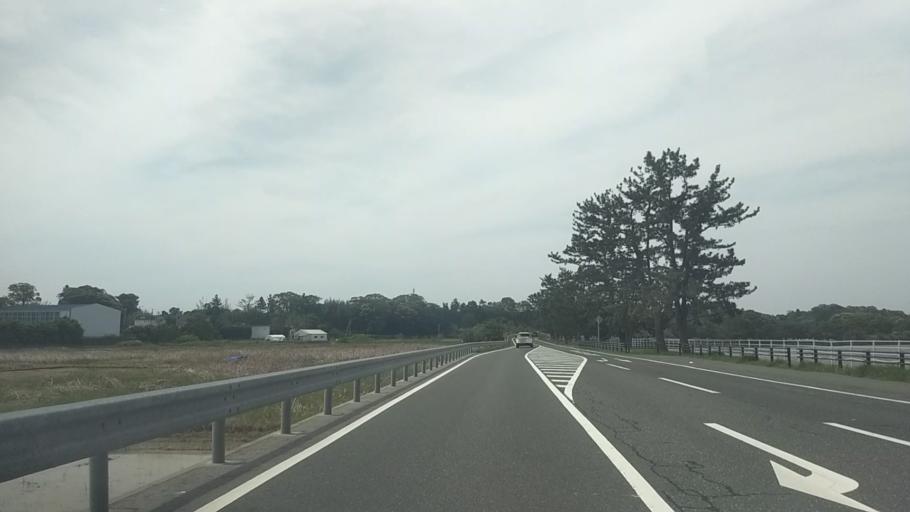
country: JP
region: Shizuoka
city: Kosai-shi
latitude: 34.7745
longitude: 137.5630
